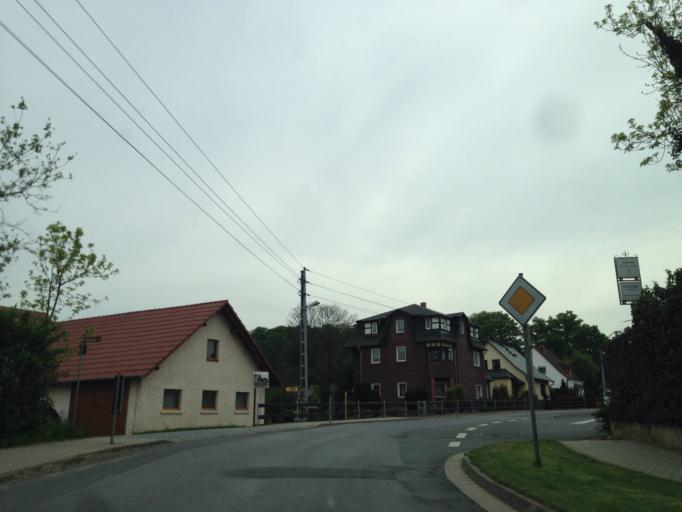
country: DE
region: Thuringia
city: Konitz
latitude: 50.6559
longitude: 11.4913
